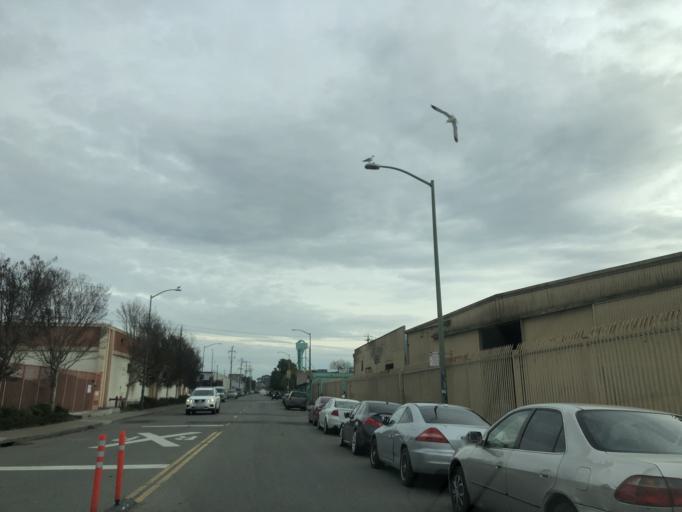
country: US
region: California
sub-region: Alameda County
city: San Leandro
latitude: 37.7340
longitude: -122.1792
